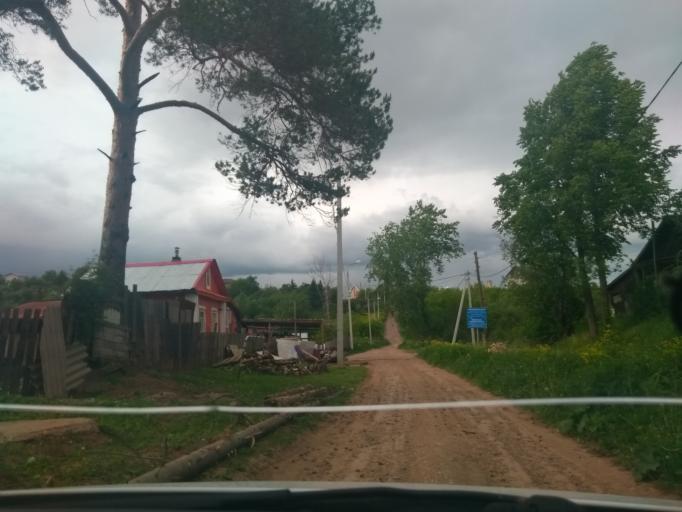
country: RU
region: Perm
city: Perm
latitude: 57.9893
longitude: 56.3371
